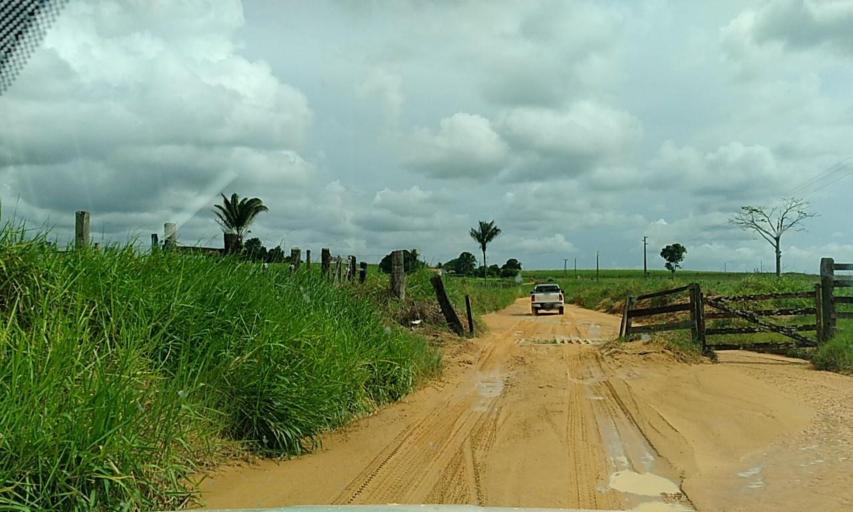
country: BR
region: Para
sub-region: Altamira
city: Altamira
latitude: -3.2499
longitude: -52.6942
